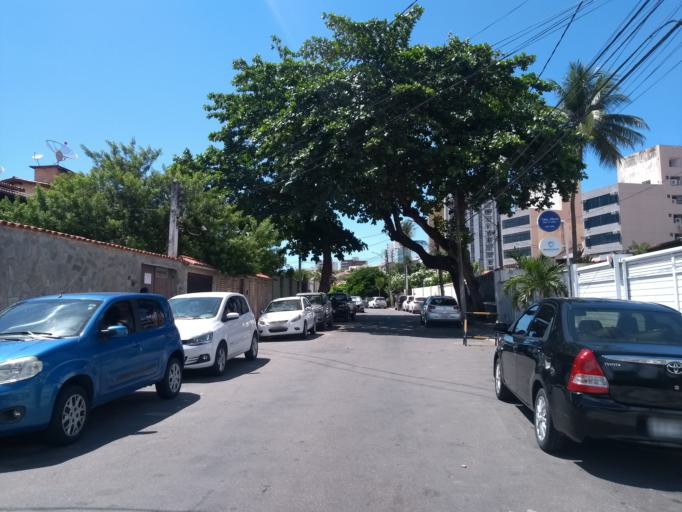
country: BR
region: Bahia
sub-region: Salvador
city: Salvador
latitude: -12.9920
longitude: -38.4606
